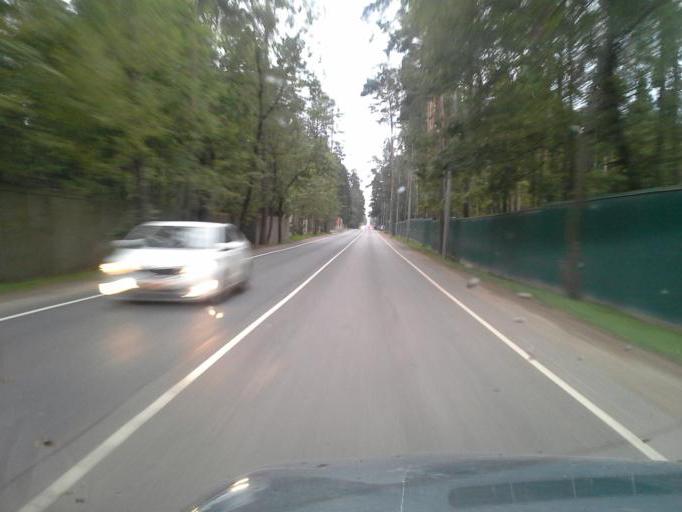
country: RU
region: Moskovskaya
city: Nazar'yevo
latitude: 55.7024
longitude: 37.0622
